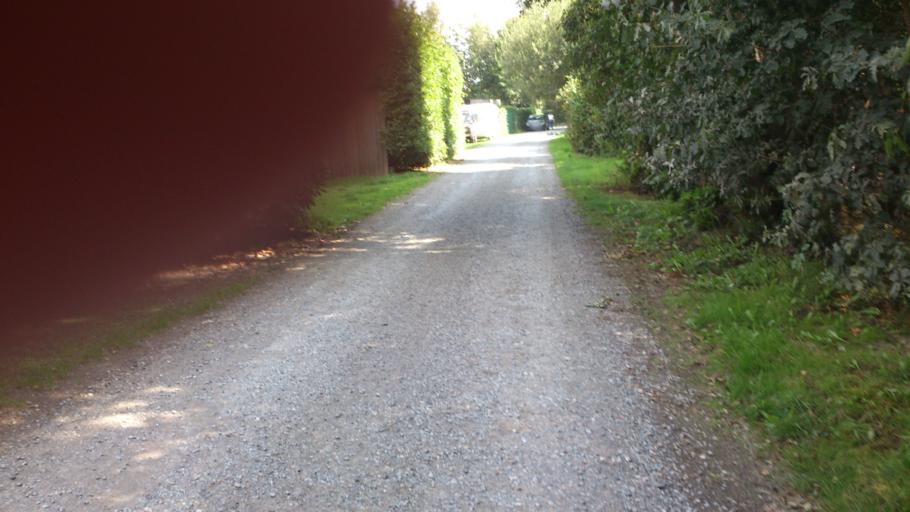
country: BE
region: Flanders
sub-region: Provincie Antwerpen
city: Dessel
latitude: 51.2167
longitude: 5.1193
